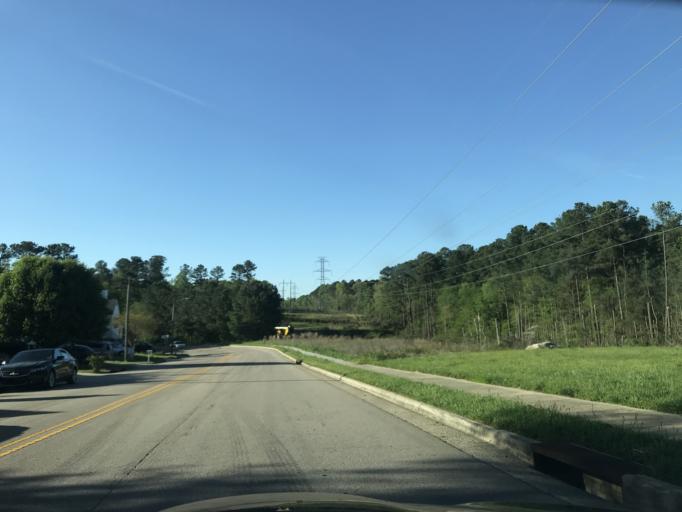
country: US
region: North Carolina
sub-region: Wake County
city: Raleigh
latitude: 35.8422
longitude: -78.5672
